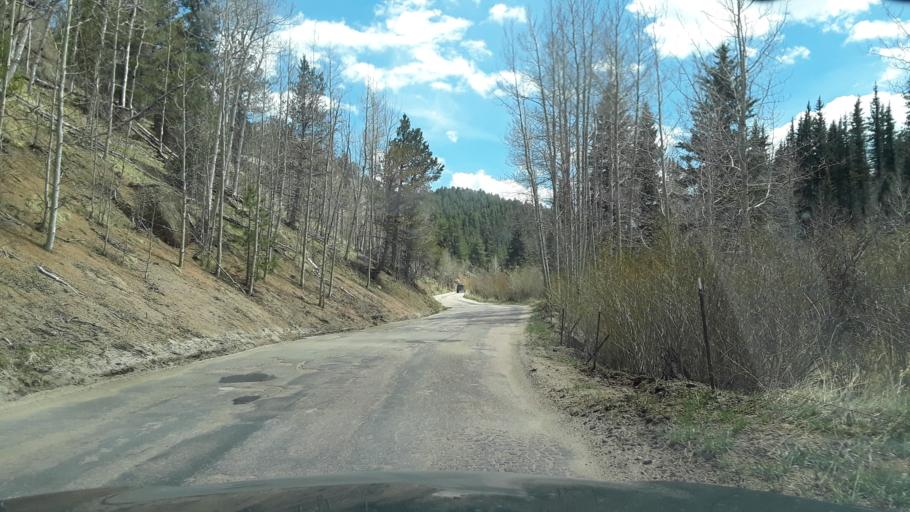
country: US
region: Colorado
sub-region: Teller County
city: Woodland Park
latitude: 39.0181
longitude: -105.0256
